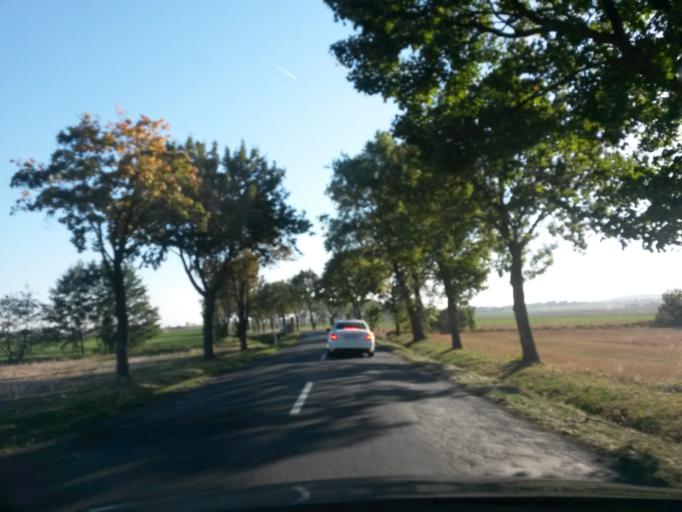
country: PL
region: Lower Silesian Voivodeship
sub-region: Powiat sredzki
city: Udanin
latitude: 51.0560
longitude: 16.4068
